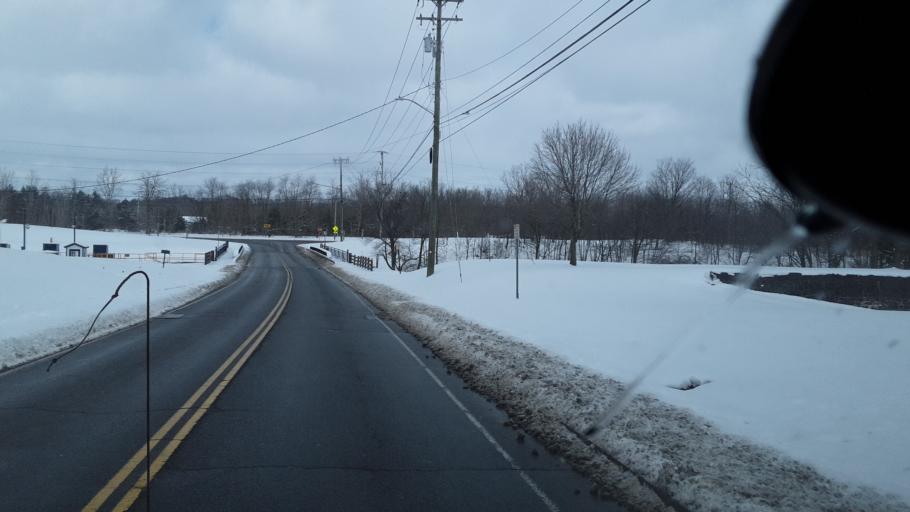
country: US
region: New York
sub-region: Wayne County
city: Newark
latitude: 43.0461
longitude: -77.0840
